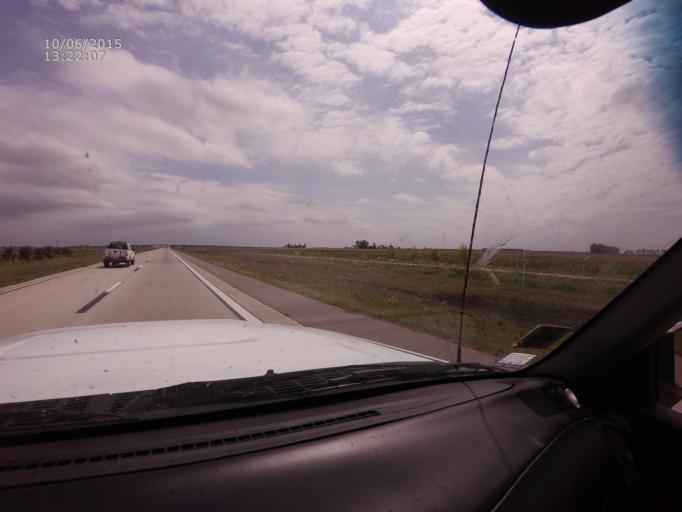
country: AR
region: Cordoba
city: Marcos Juarez
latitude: -32.6657
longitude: -62.0886
